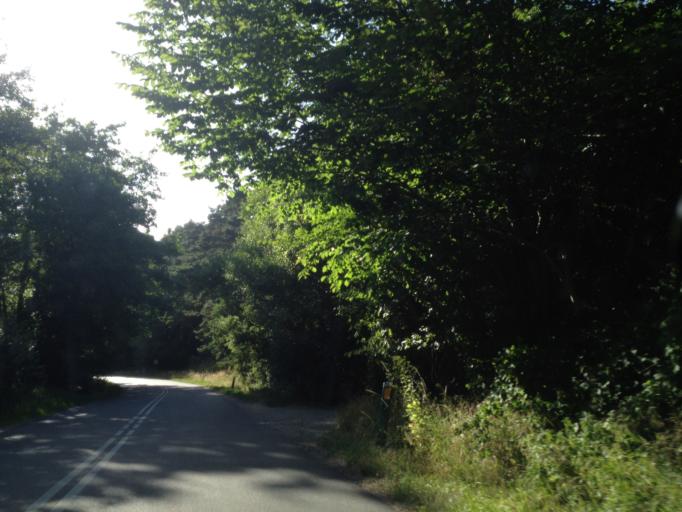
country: DK
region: Capital Region
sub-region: Halsnaes Kommune
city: Frederiksvaerk
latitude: 56.0294
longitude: 12.0895
